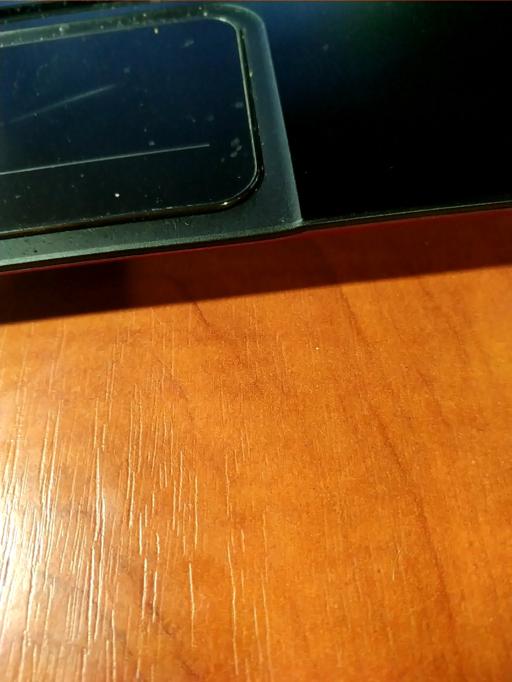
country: RU
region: Tverskaya
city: Zubtsov
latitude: 56.3323
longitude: 34.6735
